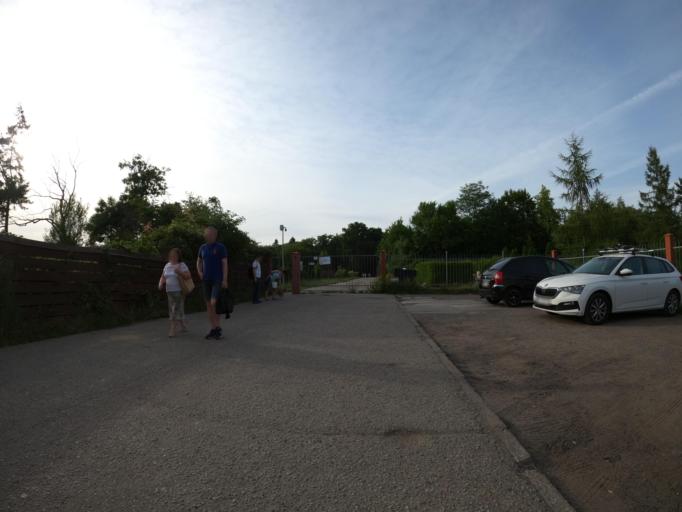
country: PL
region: West Pomeranian Voivodeship
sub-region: Szczecin
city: Szczecin
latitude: 53.4114
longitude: 14.5134
